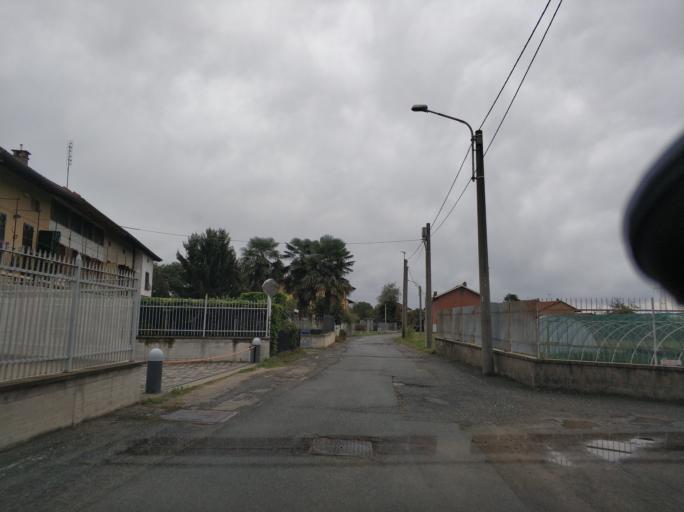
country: IT
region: Piedmont
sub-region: Provincia di Torino
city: Cirie
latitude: 45.2168
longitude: 7.6006
